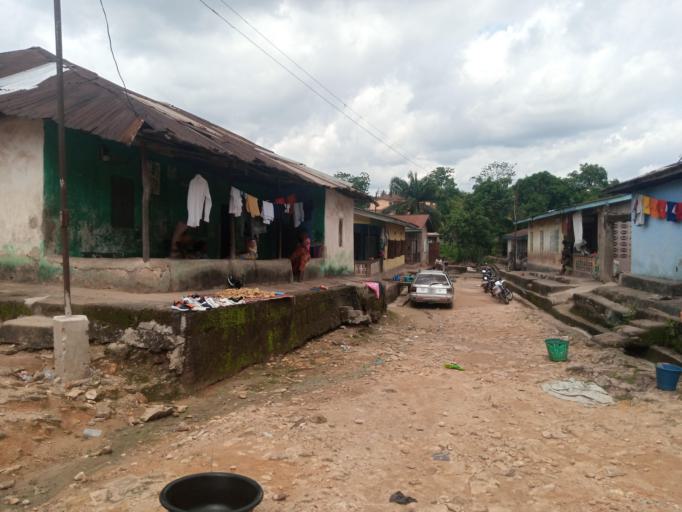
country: SL
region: Southern Province
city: Bo
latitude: 7.9738
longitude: -11.7362
